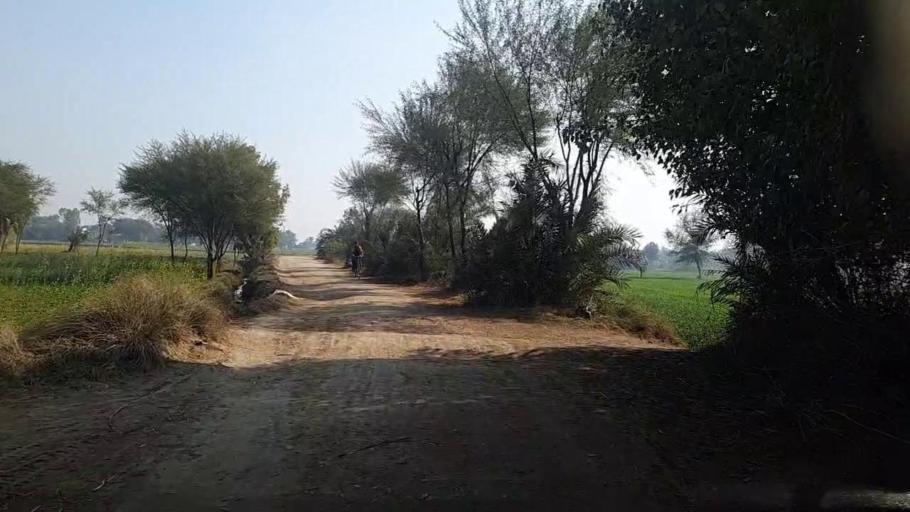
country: PK
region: Sindh
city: Khairpur
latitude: 27.9374
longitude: 69.6721
